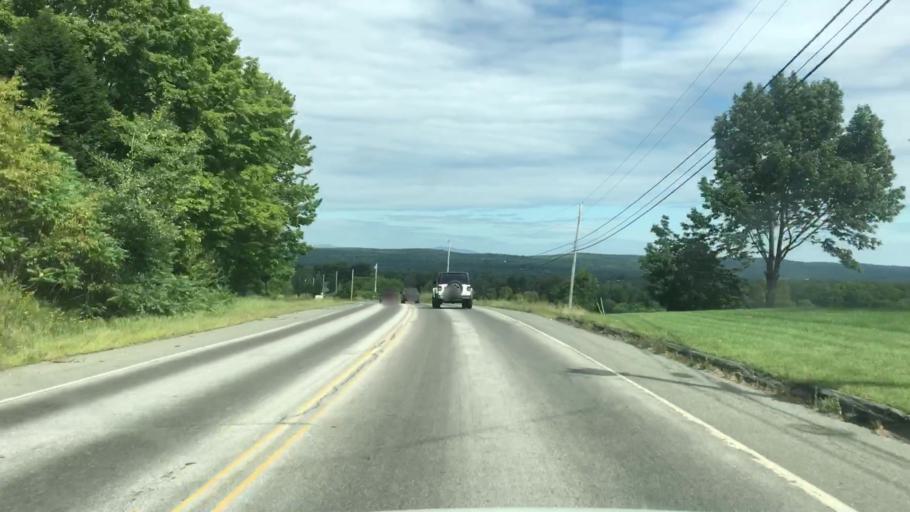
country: US
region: Maine
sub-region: Piscataquis County
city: Dover-Foxcroft
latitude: 45.1642
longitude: -69.2307
